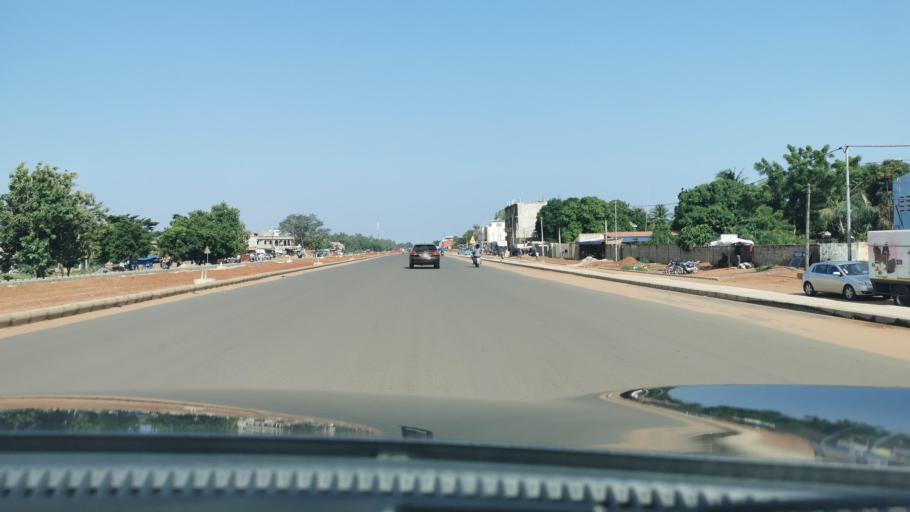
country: TG
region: Maritime
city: Lome
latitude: 6.1956
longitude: 1.1545
